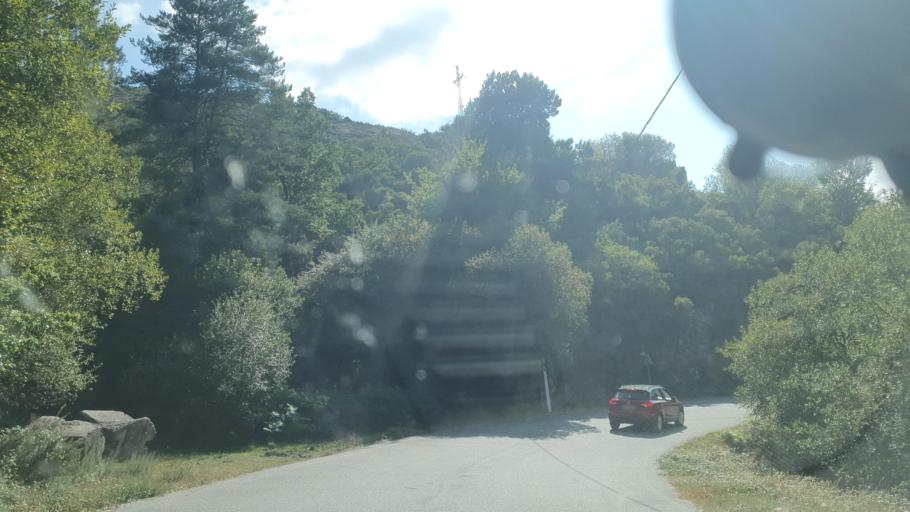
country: PT
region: Braga
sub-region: Terras de Bouro
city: Antas
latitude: 41.7620
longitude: -8.2067
